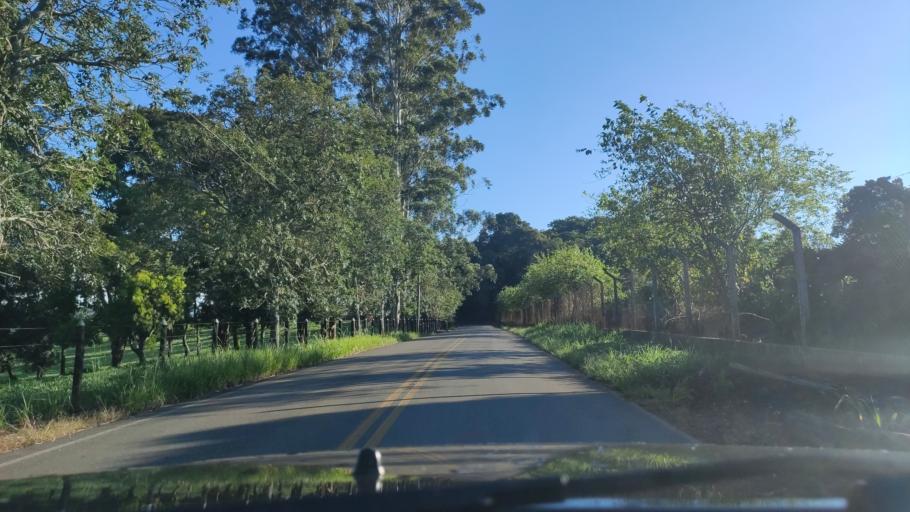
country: BR
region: Sao Paulo
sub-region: Serra Negra
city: Serra Negra
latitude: -22.5883
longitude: -46.6244
